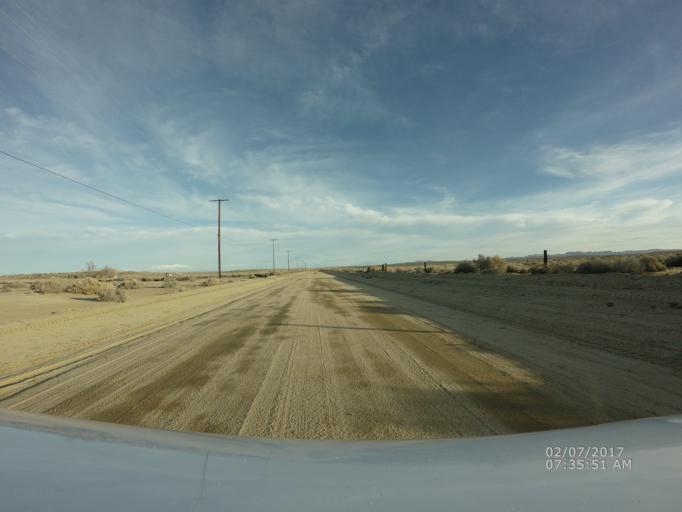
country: US
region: California
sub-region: Los Angeles County
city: Lake Los Angeles
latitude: 34.5976
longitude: -117.7201
